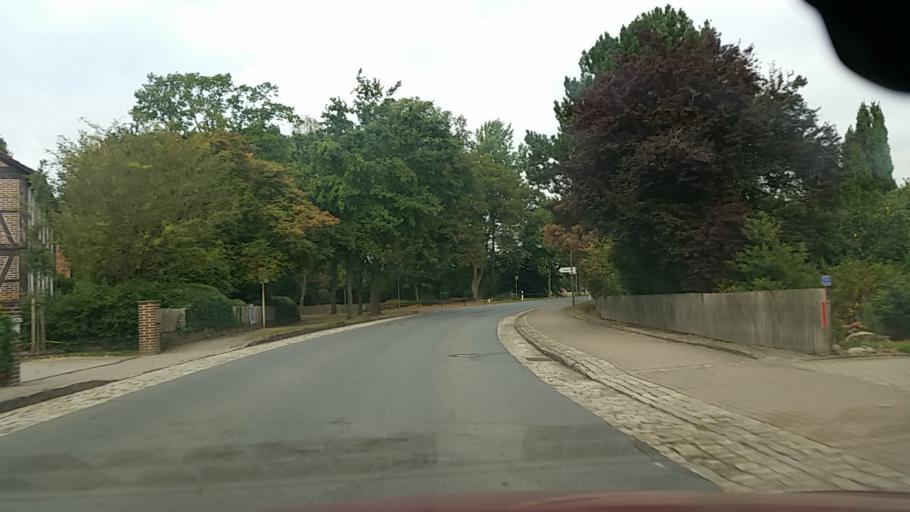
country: DE
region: Lower Saxony
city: Hohne
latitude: 52.5891
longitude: 10.3673
